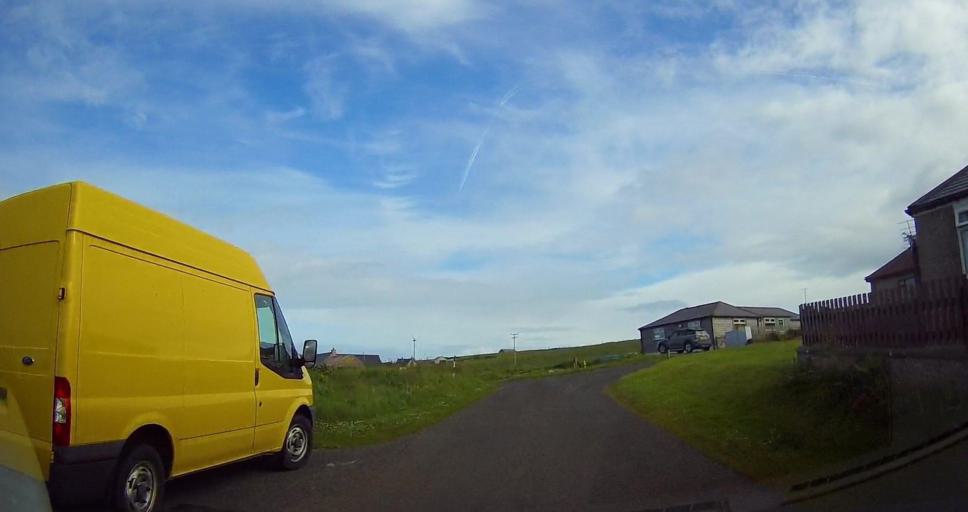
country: GB
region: Scotland
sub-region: Orkney Islands
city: Stromness
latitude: 58.7815
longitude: -3.2352
